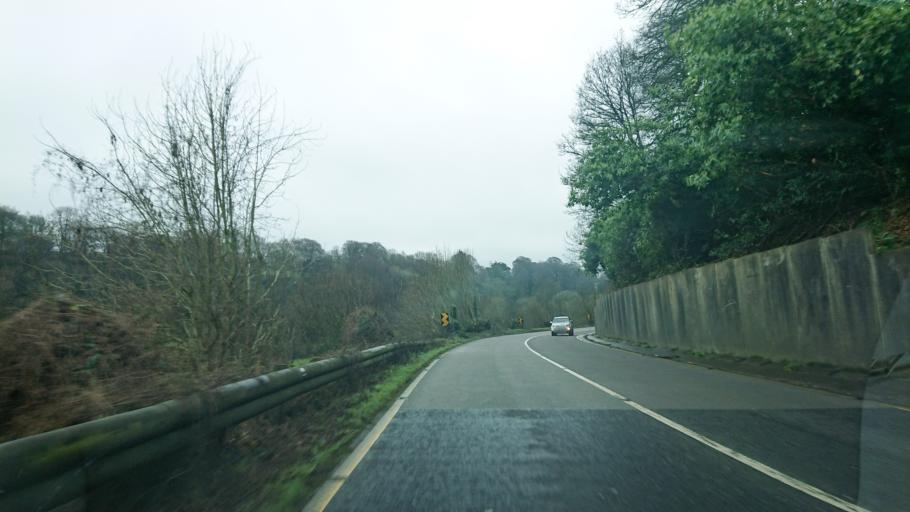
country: IE
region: Munster
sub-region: County Cork
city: Bandon
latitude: 51.7681
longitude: -8.6750
